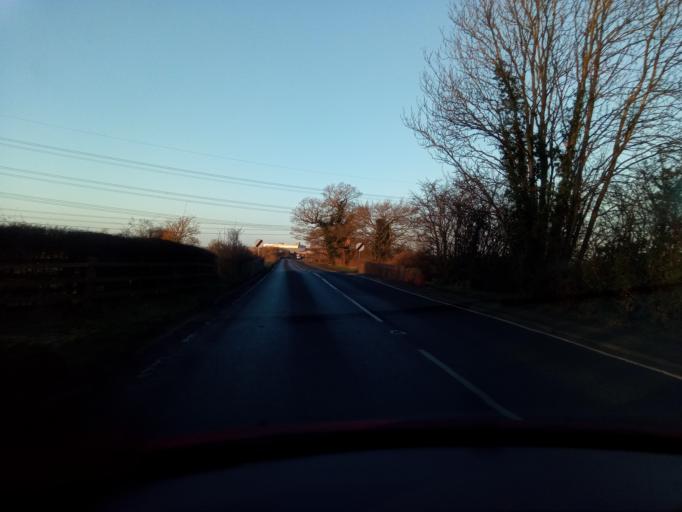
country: GB
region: England
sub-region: Leicestershire
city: Loughborough
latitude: 52.7802
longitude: -1.1829
